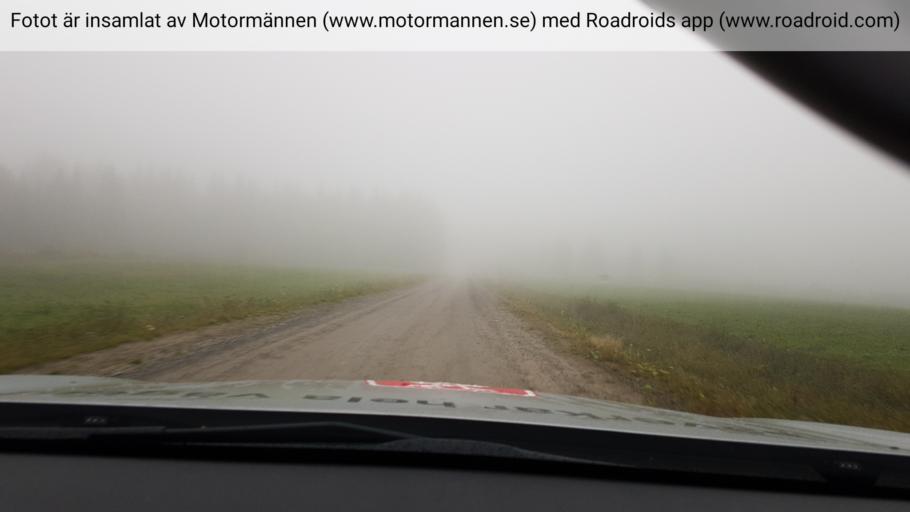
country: SE
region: Vaesterbotten
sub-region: Umea Kommun
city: Roback
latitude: 64.0861
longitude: 20.1055
